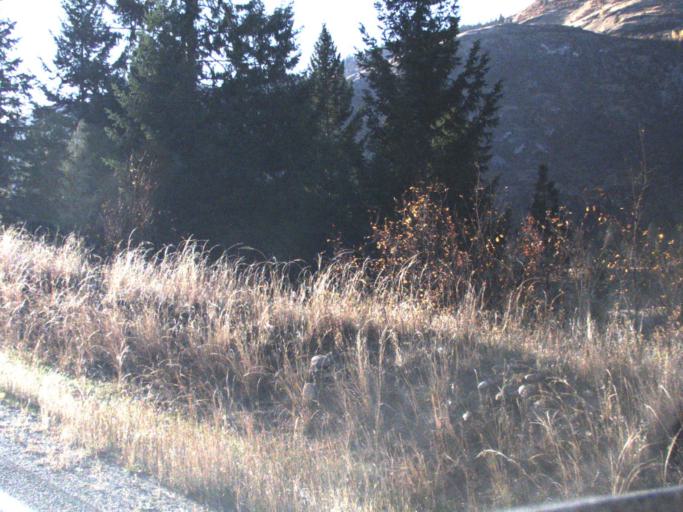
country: CA
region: British Columbia
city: Rossland
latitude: 48.8888
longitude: -117.8268
